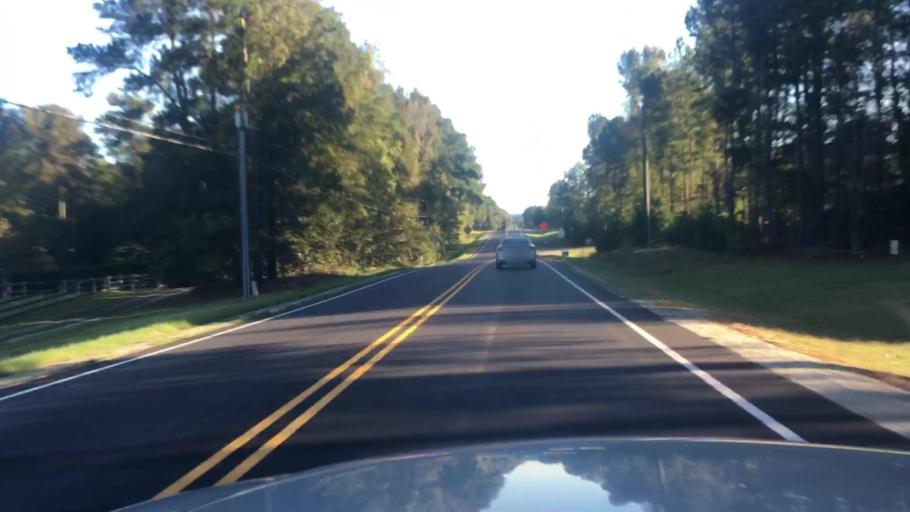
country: US
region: North Carolina
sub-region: Harnett County
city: Walkertown
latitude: 35.3356
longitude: -78.8595
